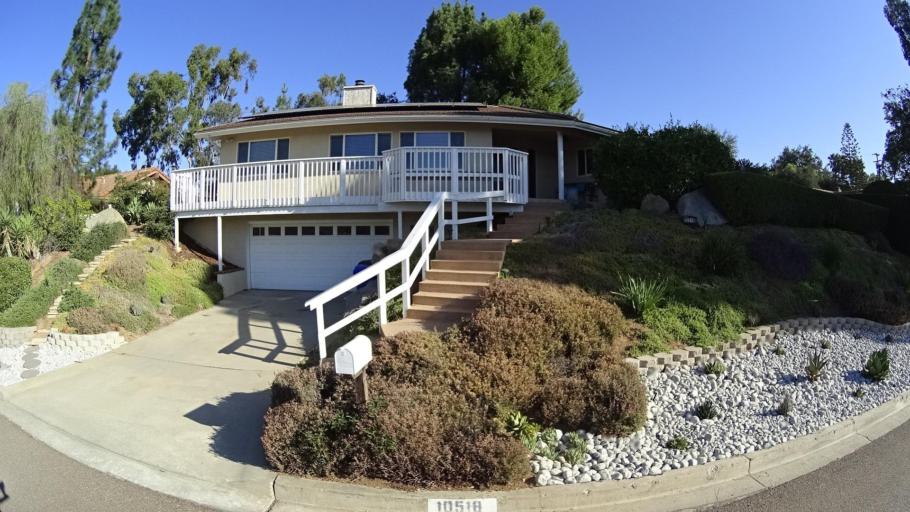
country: US
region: California
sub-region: San Diego County
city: Hidden Meadows
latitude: 33.2187
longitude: -117.1051
